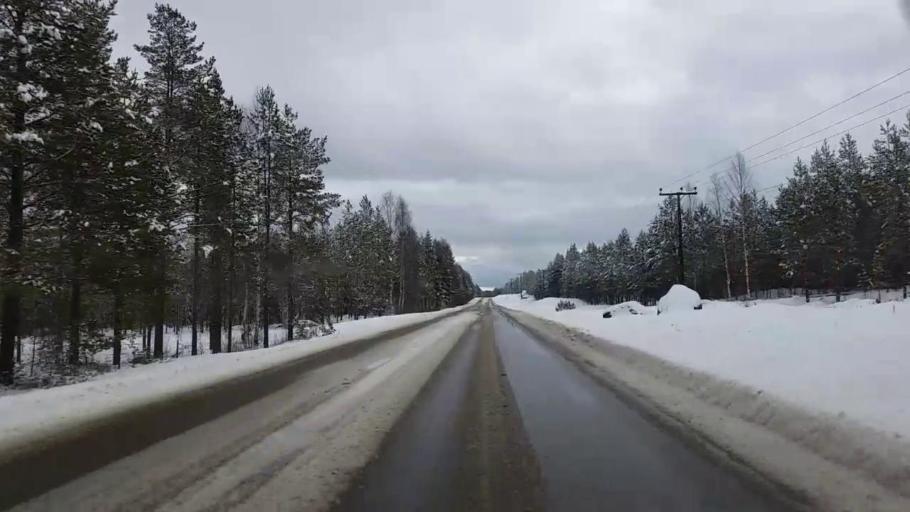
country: SE
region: Jaemtland
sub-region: Harjedalens Kommun
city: Sveg
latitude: 62.0990
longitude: 15.0760
